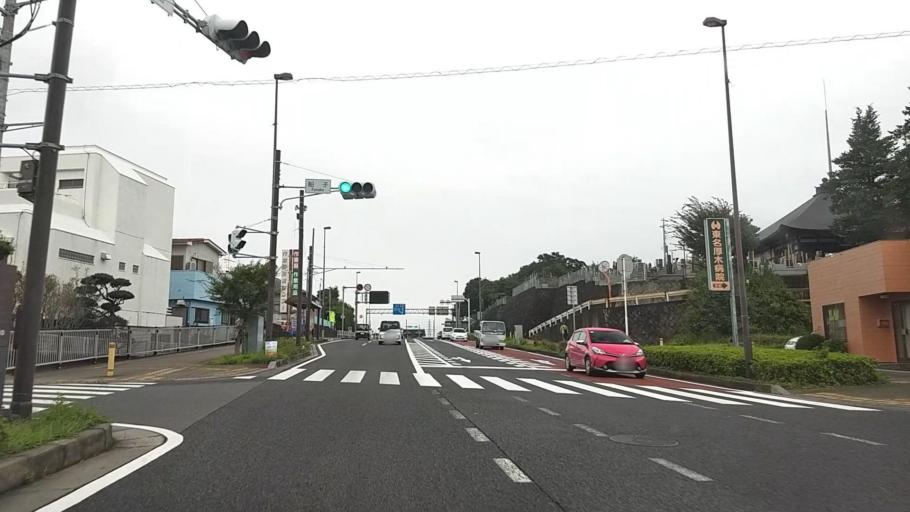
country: JP
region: Kanagawa
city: Atsugi
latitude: 35.4270
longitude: 139.3510
